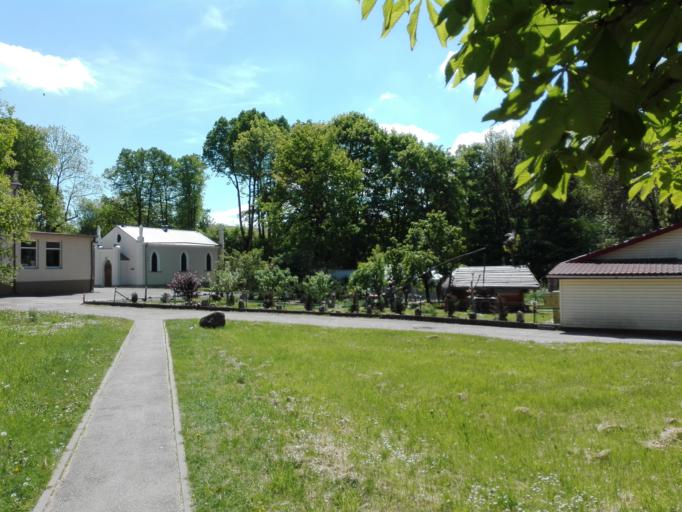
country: LT
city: Grigiskes
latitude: 54.6299
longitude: 25.1064
